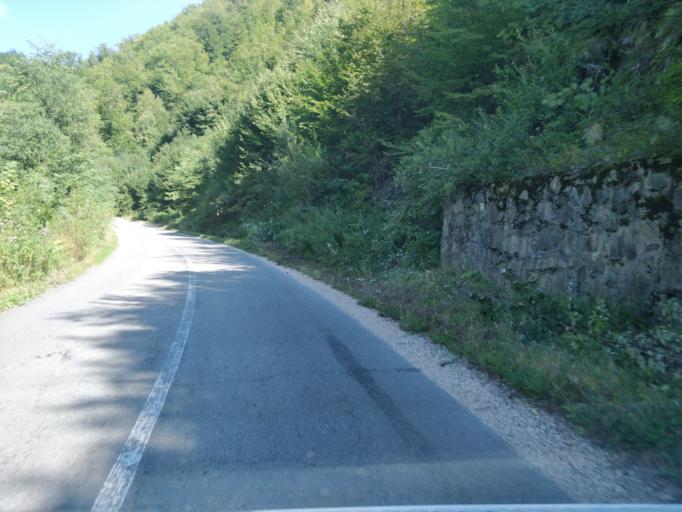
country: RO
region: Cluj
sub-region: Comuna Sacueu
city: Sacuieu
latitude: 46.8405
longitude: 22.8629
